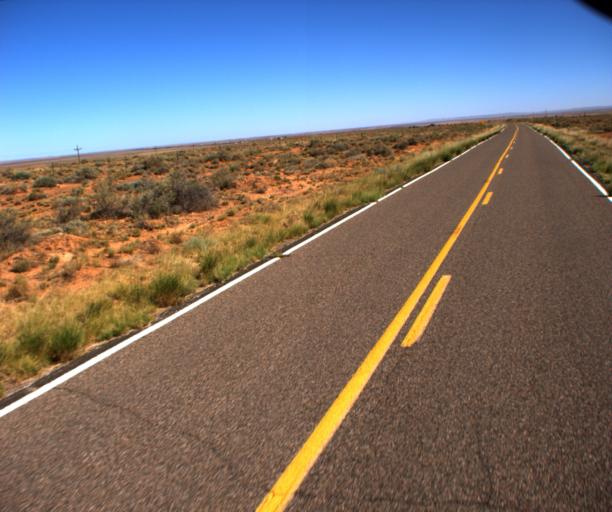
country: US
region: Arizona
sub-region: Coconino County
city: LeChee
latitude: 35.1027
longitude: -110.8638
